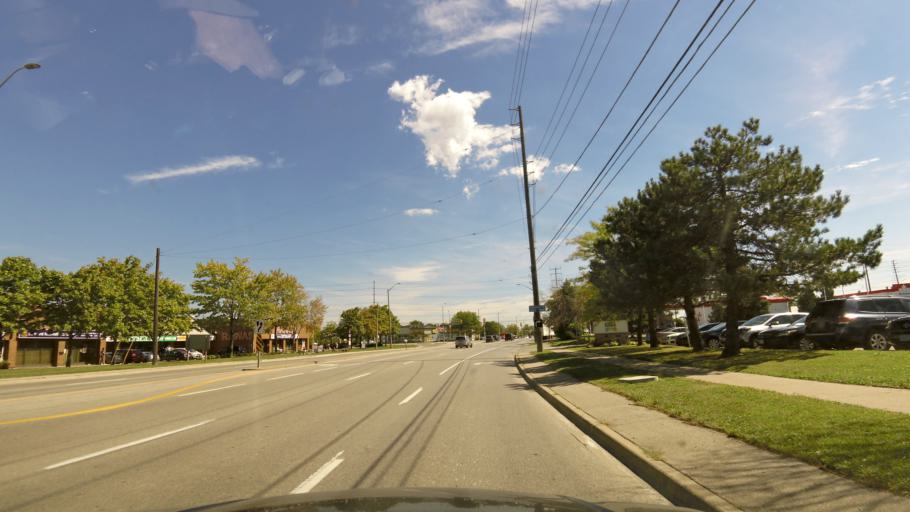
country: CA
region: Ontario
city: Mississauga
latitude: 43.6278
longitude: -79.6319
